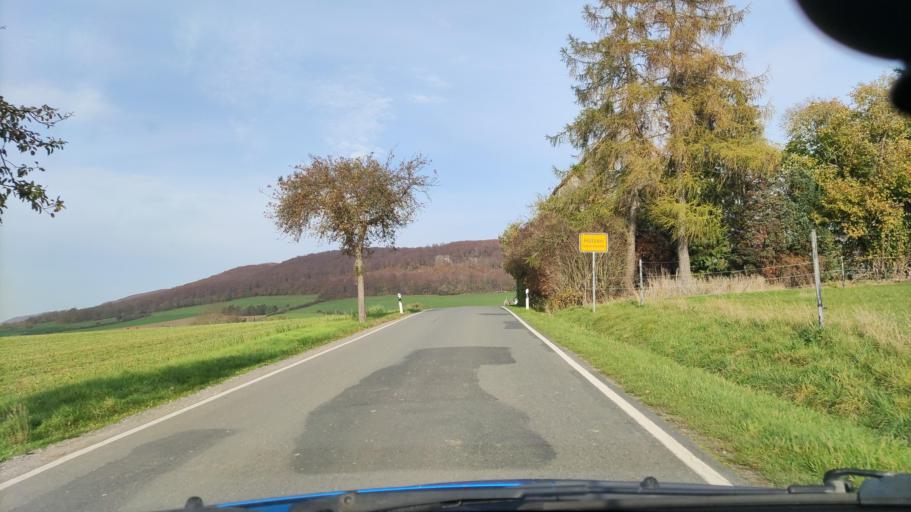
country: DE
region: Lower Saxony
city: Holzen
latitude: 51.9303
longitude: 9.6661
